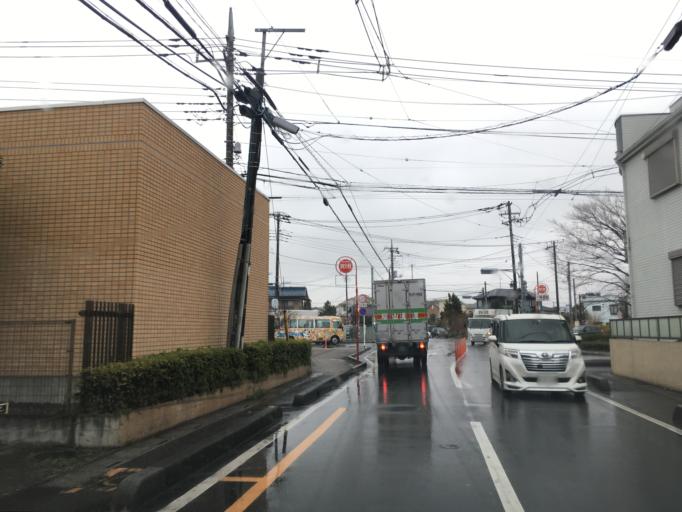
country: JP
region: Saitama
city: Koshigaya
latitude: 35.8904
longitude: 139.7802
